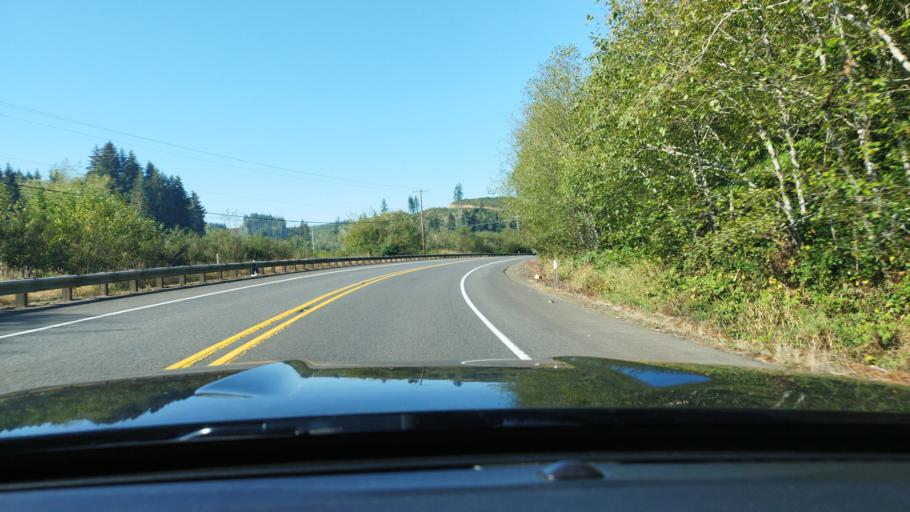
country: US
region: Oregon
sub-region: Clatsop County
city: Astoria
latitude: 46.1655
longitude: -123.7463
